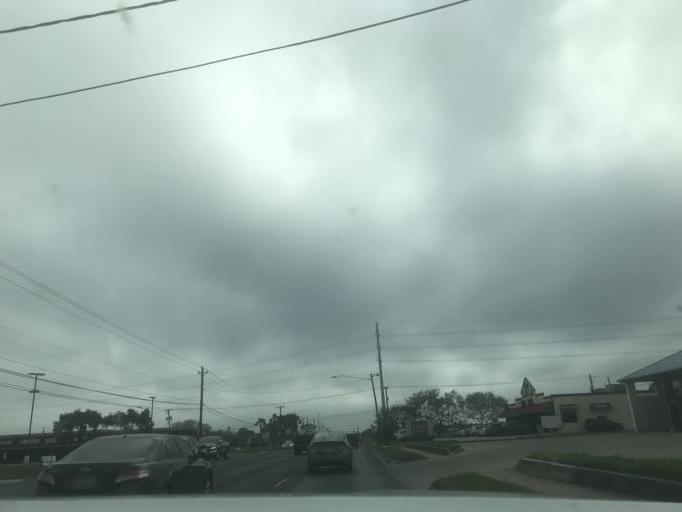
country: US
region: Texas
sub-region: Nueces County
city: Corpus Christi
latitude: 27.6894
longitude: -97.3636
